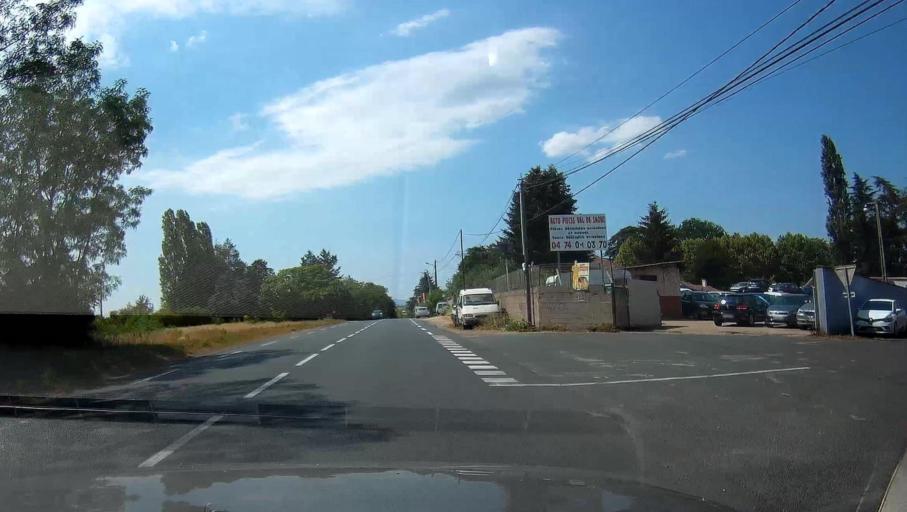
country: FR
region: Rhone-Alpes
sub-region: Departement de l'Ain
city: Saint-Didier-de-Formans
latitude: 45.9328
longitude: 4.7975
